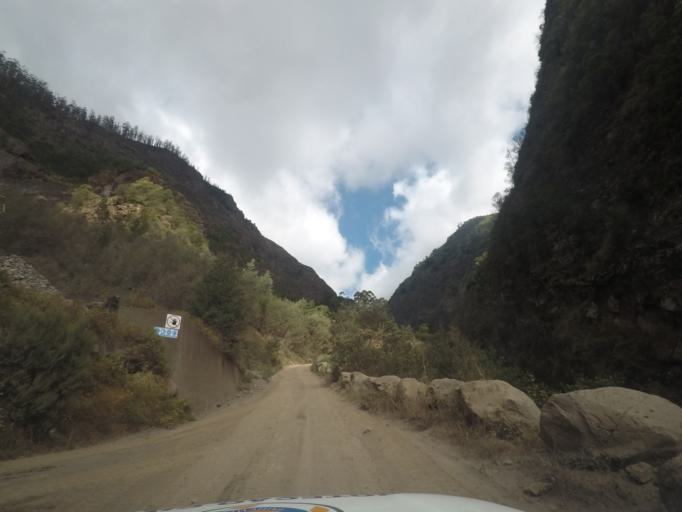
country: PT
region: Madeira
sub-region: Funchal
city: Nossa Senhora do Monte
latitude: 32.6888
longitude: -16.9166
